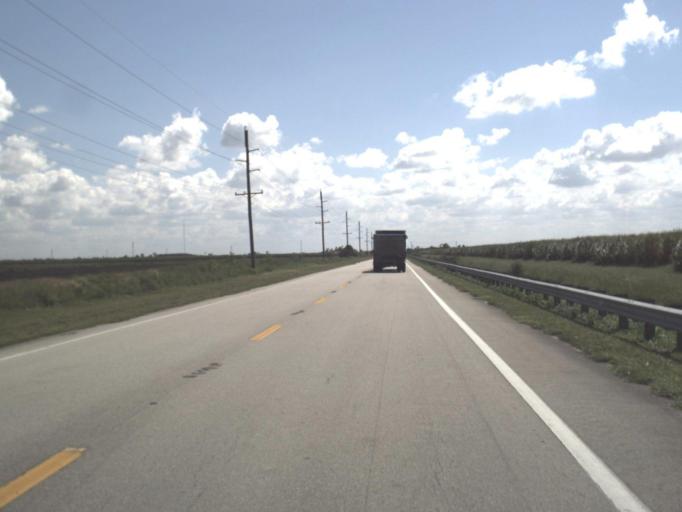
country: US
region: Florida
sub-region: Glades County
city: Moore Haven
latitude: 26.8622
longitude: -81.1228
